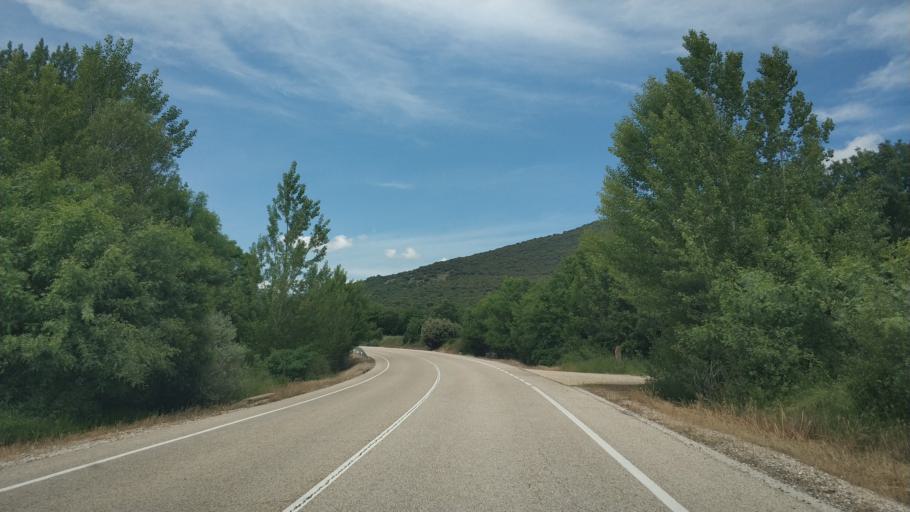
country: ES
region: Castille and Leon
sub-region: Provincia de Soria
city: Sotillo del Rincon
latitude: 41.8844
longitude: -2.6101
